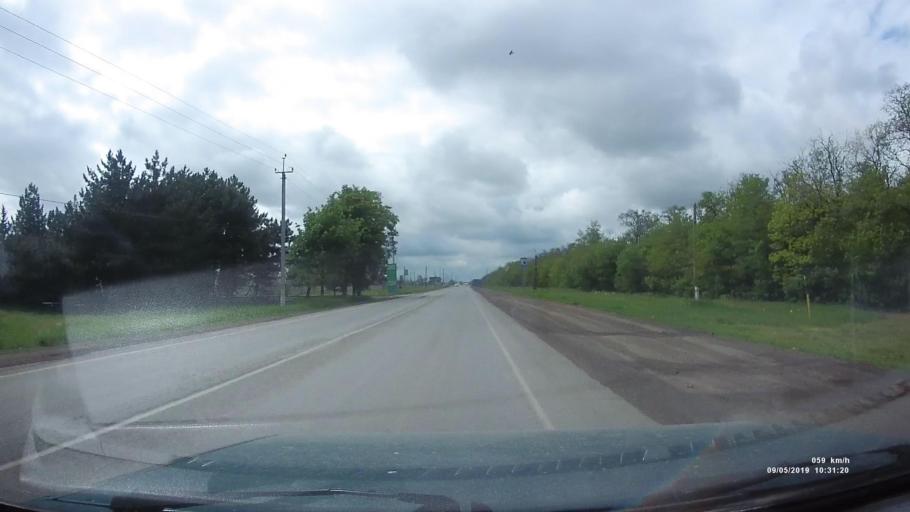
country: RU
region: Rostov
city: Azov
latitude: 47.0828
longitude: 39.4280
